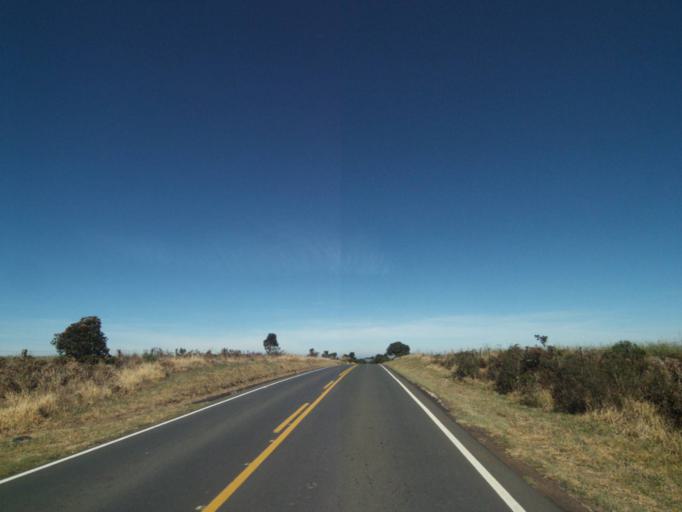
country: BR
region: Parana
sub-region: Castro
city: Castro
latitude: -24.7385
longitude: -50.1825
